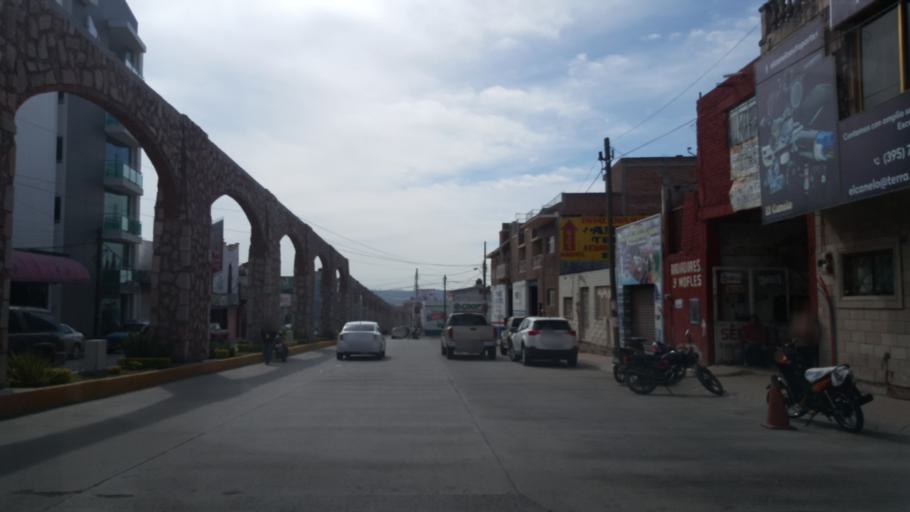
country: MX
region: Jalisco
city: San Juan de los Lagos
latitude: 21.2519
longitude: -102.3281
